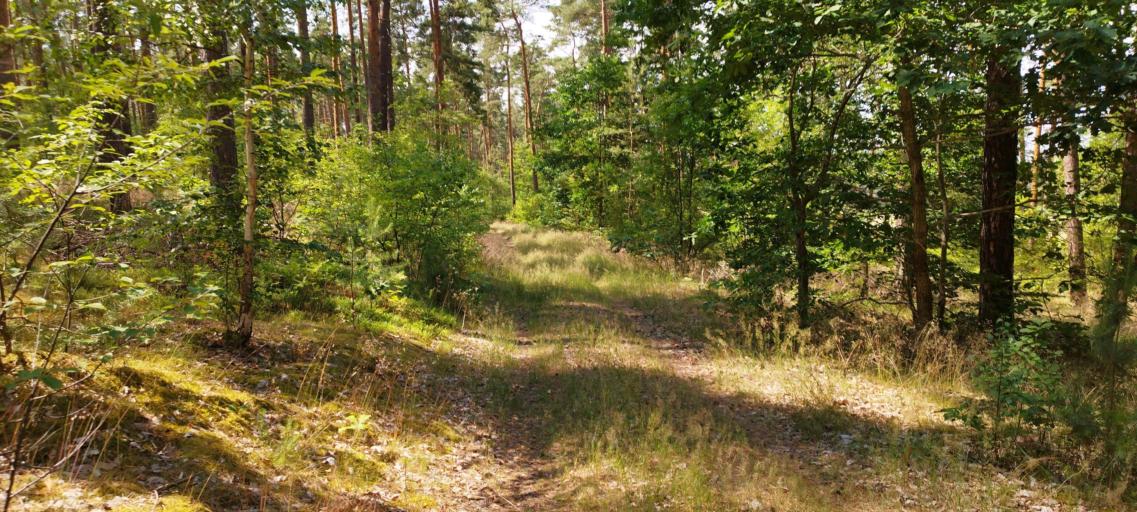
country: DE
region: Brandenburg
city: Langewahl
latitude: 52.3154
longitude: 14.1015
